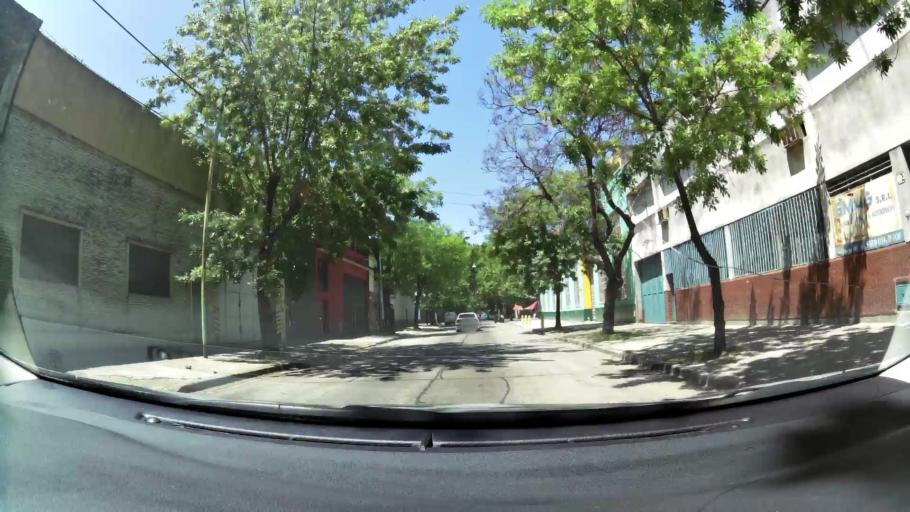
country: AR
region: Buenos Aires
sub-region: Partido de Avellaneda
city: Avellaneda
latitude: -34.6540
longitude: -58.3893
